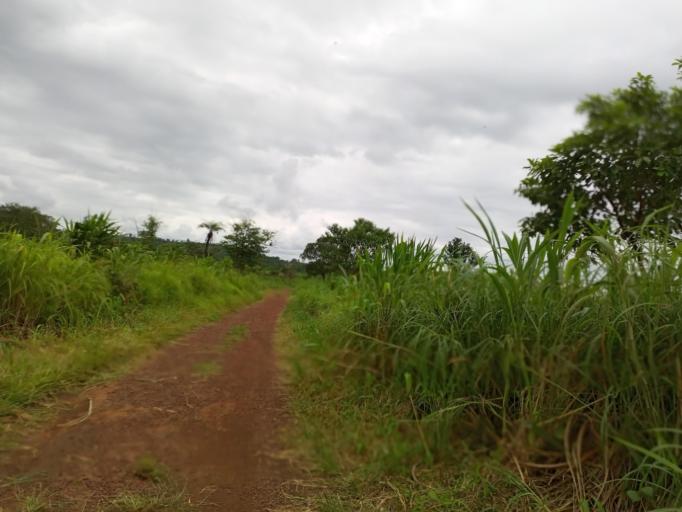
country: SL
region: Northern Province
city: Kamakwie
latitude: 9.5052
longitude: -12.2654
